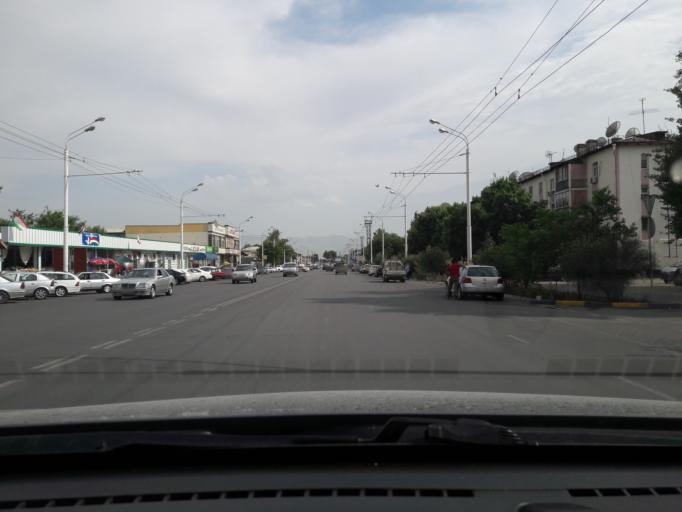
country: TJ
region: Dushanbe
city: Dushanbe
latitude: 38.5451
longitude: 68.7553
